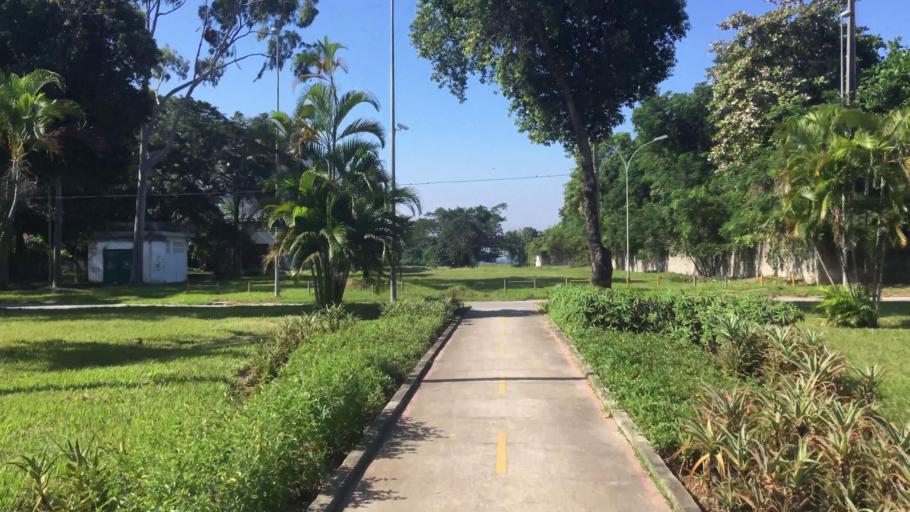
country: BR
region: Rio de Janeiro
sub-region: Rio De Janeiro
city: Rio de Janeiro
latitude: -22.8398
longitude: -43.2285
